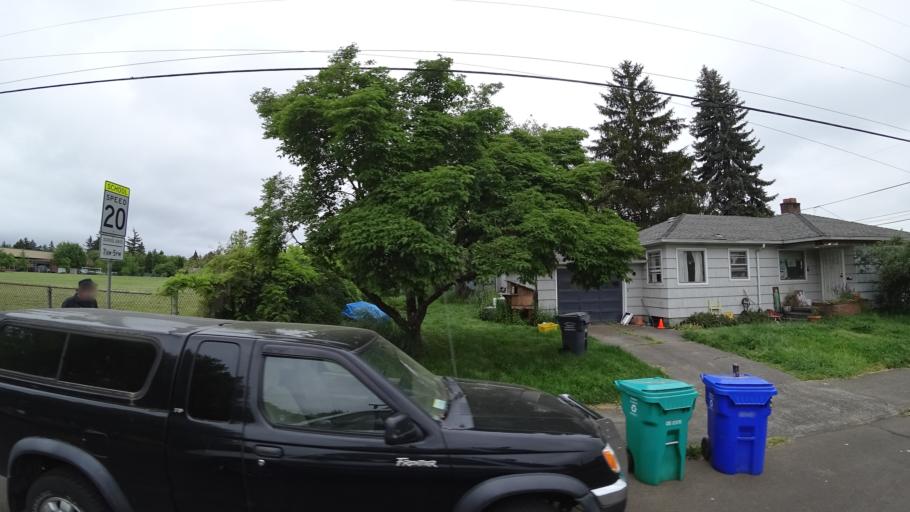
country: US
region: Oregon
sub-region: Multnomah County
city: Portland
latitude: 45.5599
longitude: -122.6214
